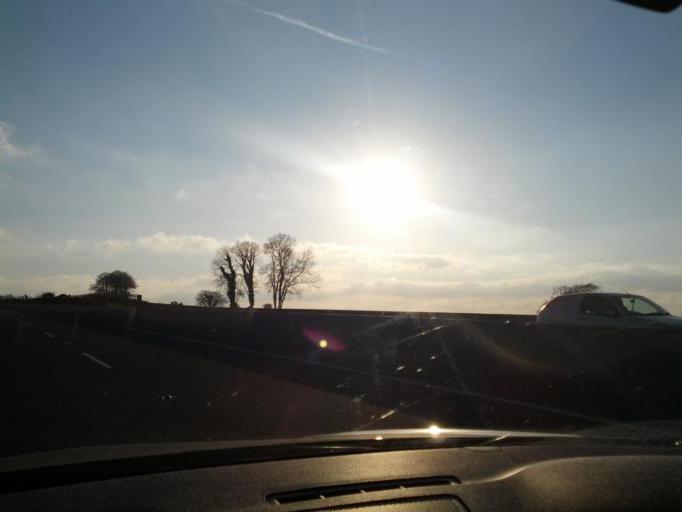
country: IE
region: Munster
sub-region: North Tipperary
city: Roscrea
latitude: 52.8994
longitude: -7.9043
